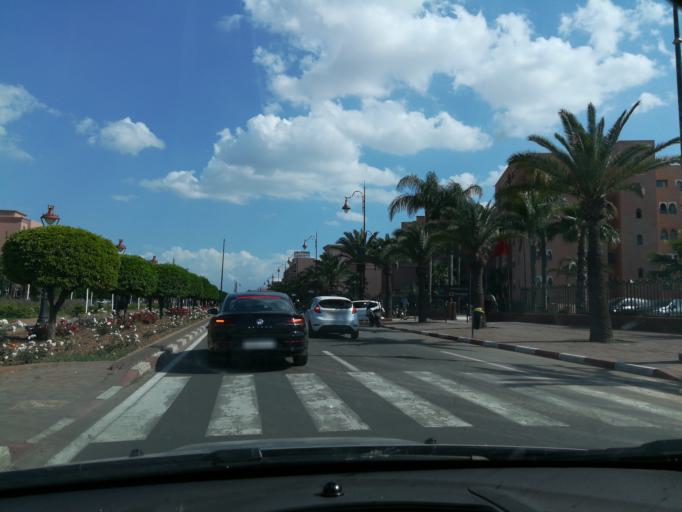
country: MA
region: Marrakech-Tensift-Al Haouz
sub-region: Marrakech
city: Marrakesh
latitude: 31.6265
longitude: -8.0139
